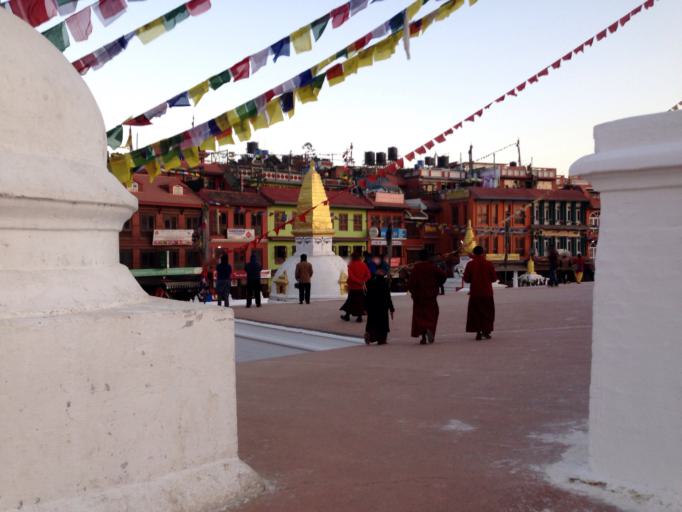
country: NP
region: Central Region
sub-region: Bagmati Zone
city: Kathmandu
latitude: 27.7218
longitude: 85.3622
